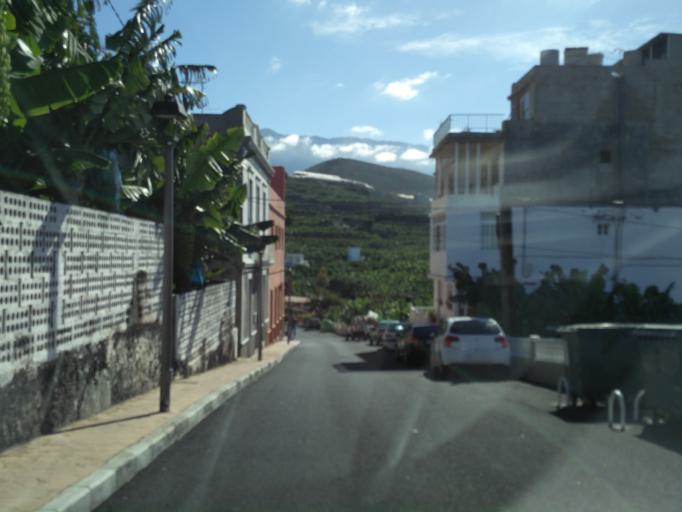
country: ES
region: Canary Islands
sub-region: Provincia de Santa Cruz de Tenerife
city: Tazacorte
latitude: 28.6377
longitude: -17.9298
